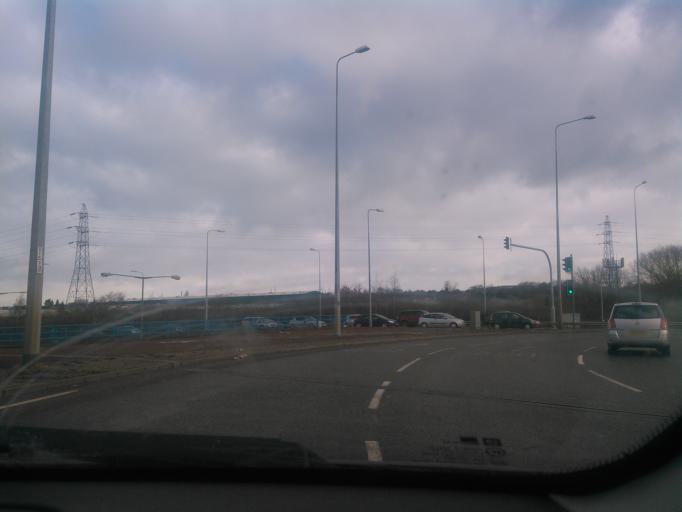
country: GB
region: England
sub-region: Stoke-on-Trent
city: Stoke-on-Trent
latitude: 52.9910
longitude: -2.1834
